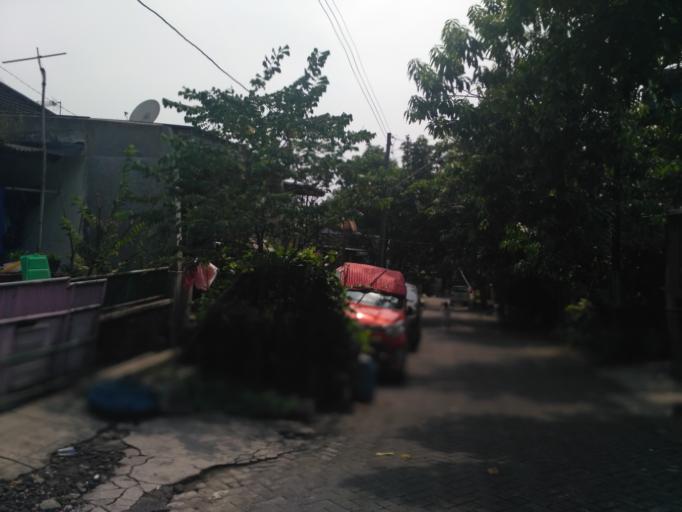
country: ID
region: Central Java
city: Mranggen
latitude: -7.0646
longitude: 110.4597
